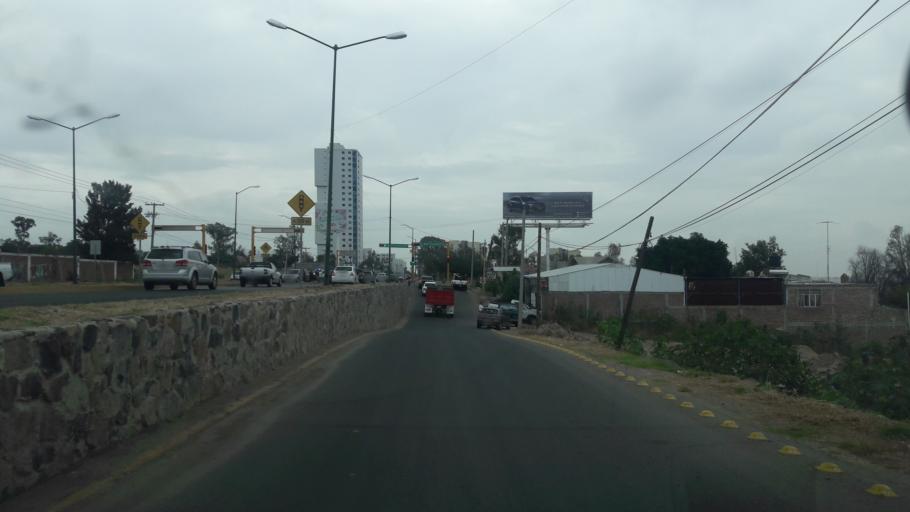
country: MX
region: Guanajuato
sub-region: Leon
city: La Ermita
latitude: 21.1618
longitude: -101.7252
